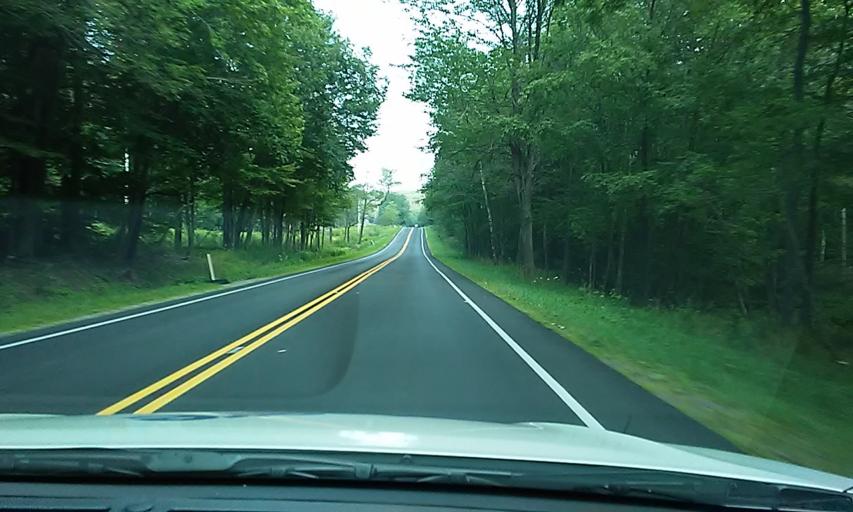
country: US
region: Pennsylvania
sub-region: Elk County
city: Saint Marys
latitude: 41.4519
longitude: -78.4391
